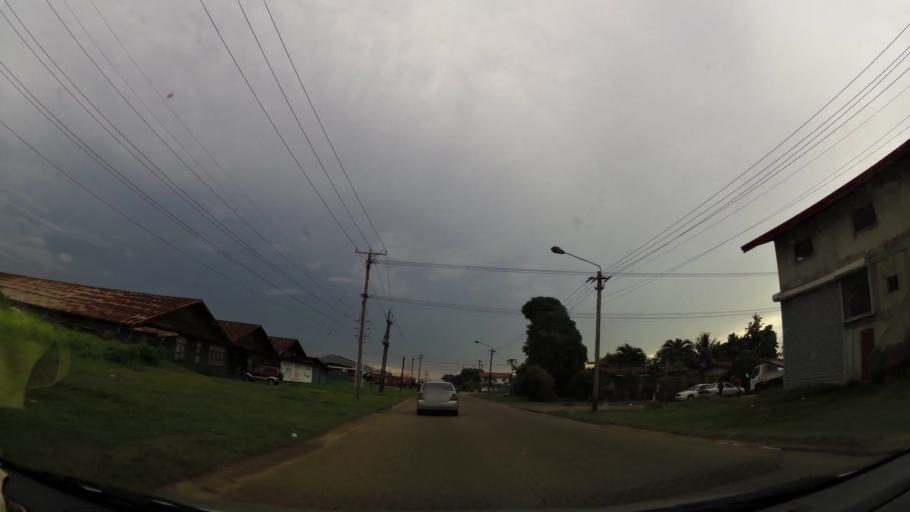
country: SR
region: Paramaribo
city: Paramaribo
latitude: 5.8046
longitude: -55.1941
